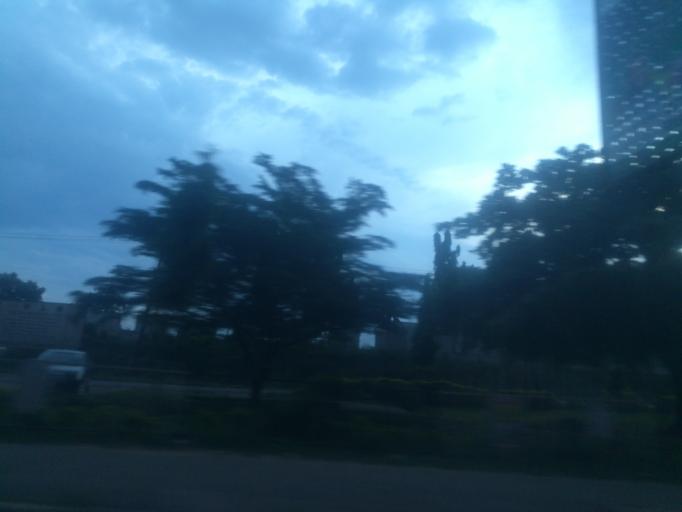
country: NG
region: Oyo
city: Ibadan
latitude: 7.3621
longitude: 3.8664
